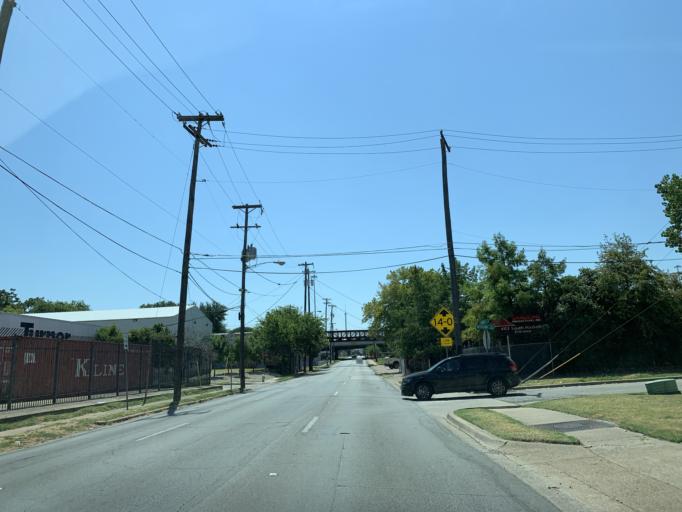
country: US
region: Texas
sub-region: Dallas County
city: Dallas
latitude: 32.7875
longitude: -96.7694
